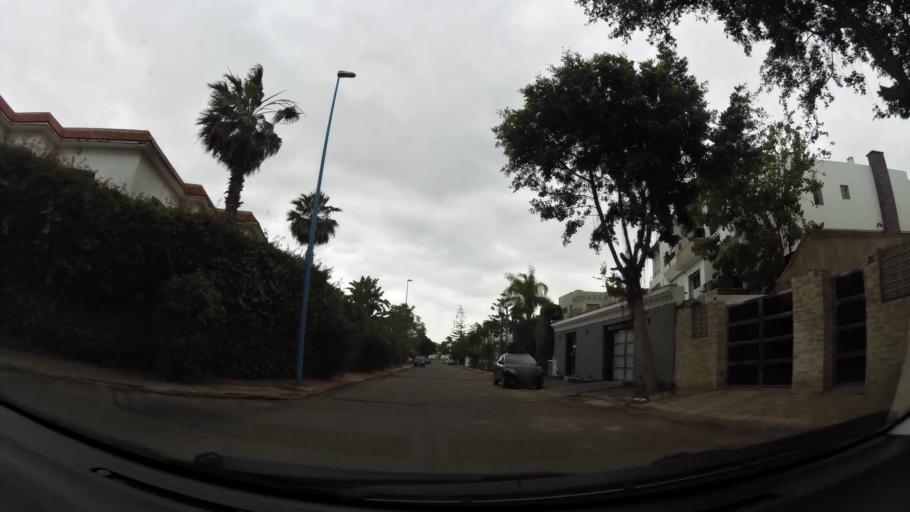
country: MA
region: Grand Casablanca
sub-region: Casablanca
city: Casablanca
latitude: 33.5971
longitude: -7.6573
